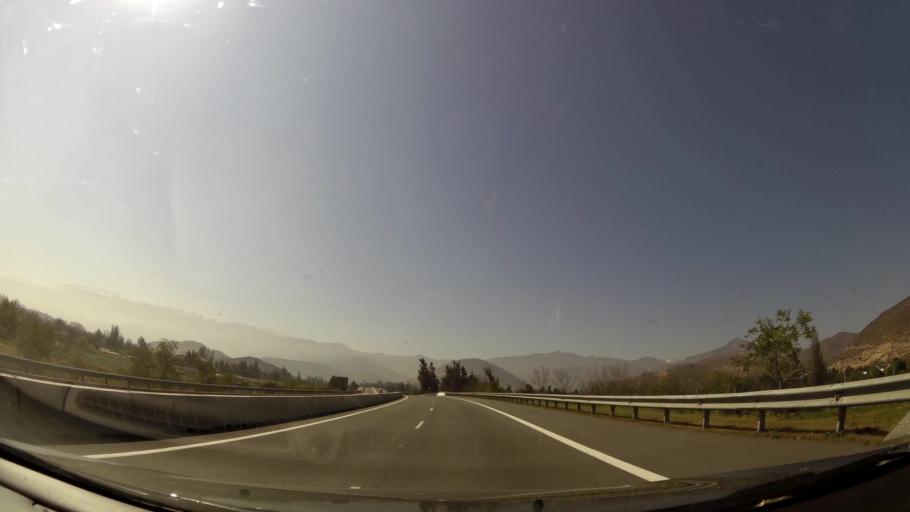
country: CL
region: Santiago Metropolitan
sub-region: Provincia de Chacabuco
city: Chicureo Abajo
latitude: -33.2993
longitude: -70.6830
